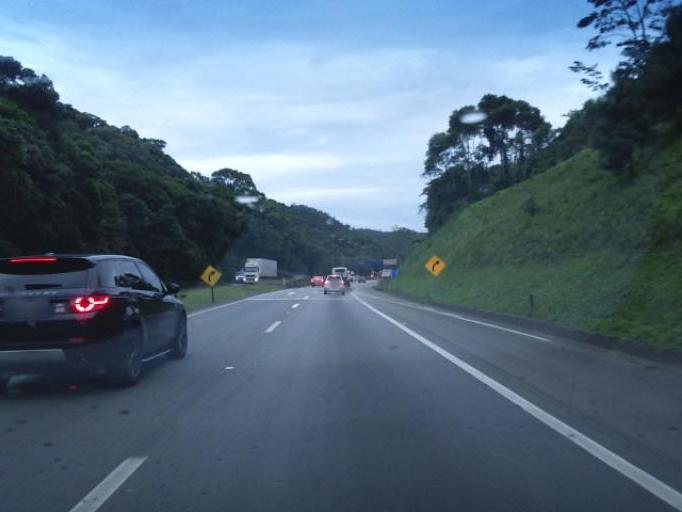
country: BR
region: Parana
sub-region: Sao Jose Dos Pinhais
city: Sao Jose dos Pinhais
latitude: -25.8535
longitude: -48.9804
